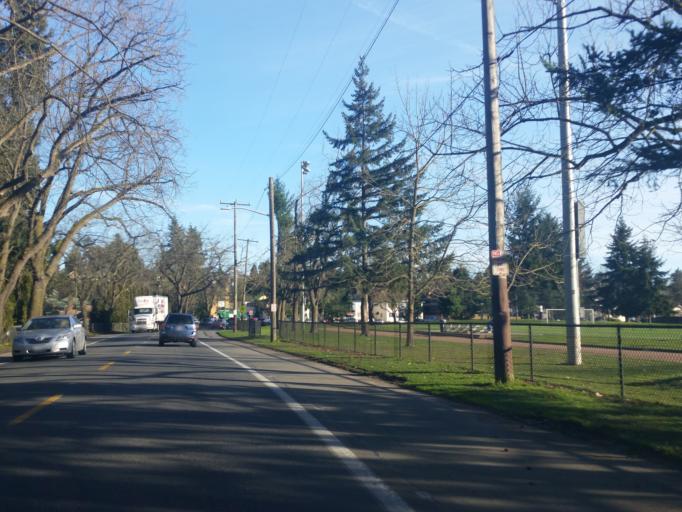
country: US
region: Washington
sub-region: King County
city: Seattle
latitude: 47.6703
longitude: -122.3421
